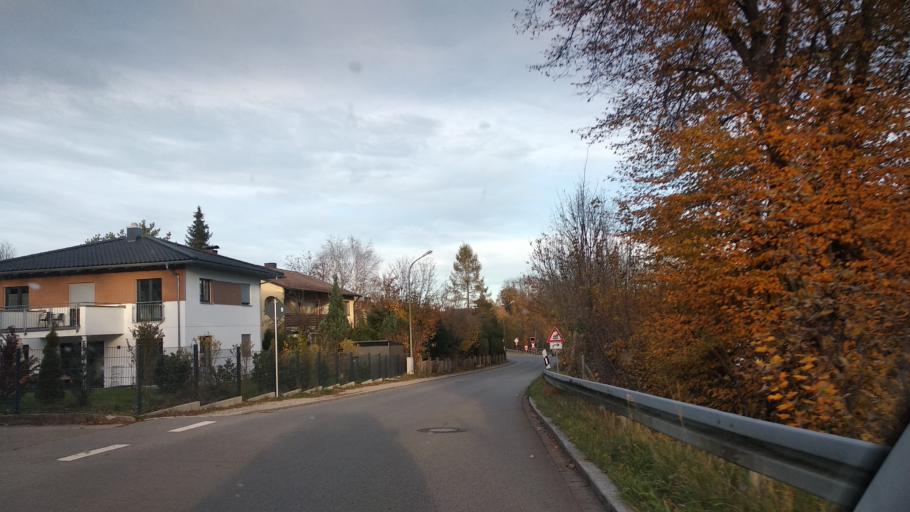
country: DE
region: Bavaria
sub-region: Upper Bavaria
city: Grafing bei Munchen
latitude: 48.0445
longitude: 11.9561
